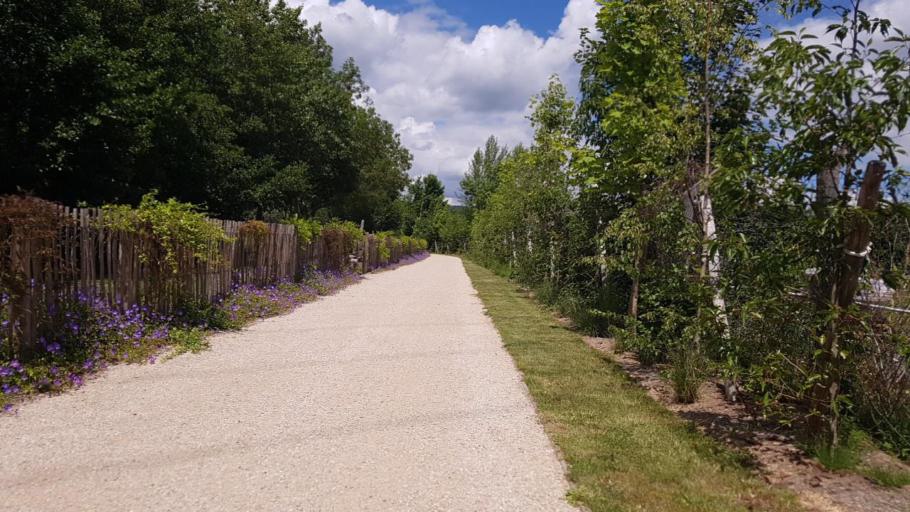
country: FR
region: Champagne-Ardenne
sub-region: Departement de la Marne
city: Dizy
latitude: 49.0578
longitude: 3.9616
